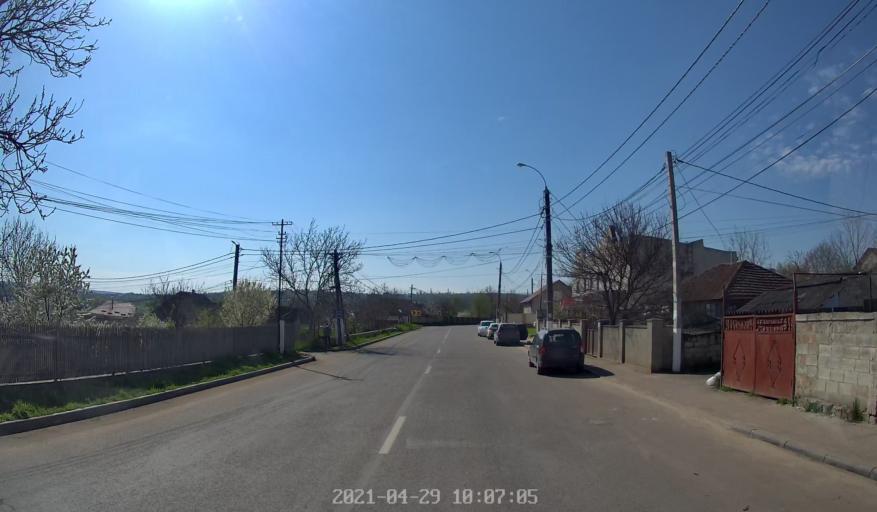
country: MD
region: Chisinau
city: Cricova
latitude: 47.1376
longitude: 28.8667
